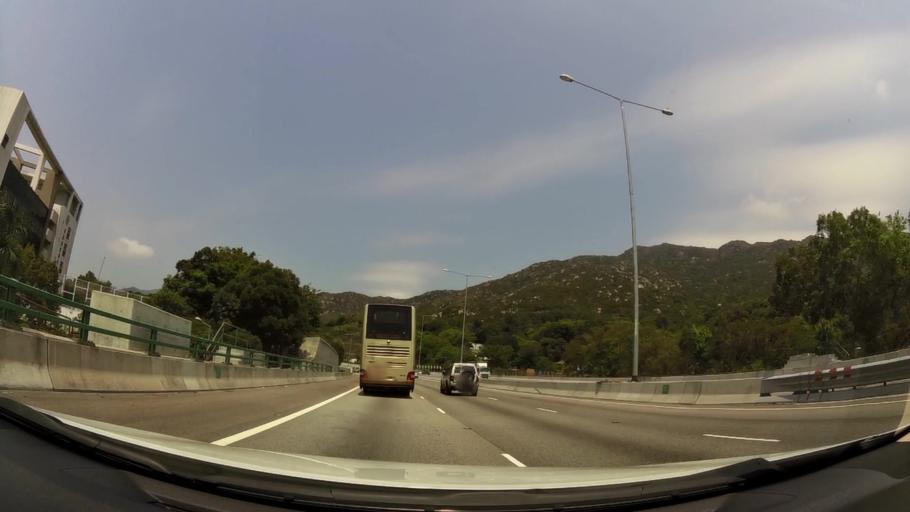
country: HK
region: Tuen Mun
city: Tuen Mun
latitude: 22.3747
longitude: 113.9966
